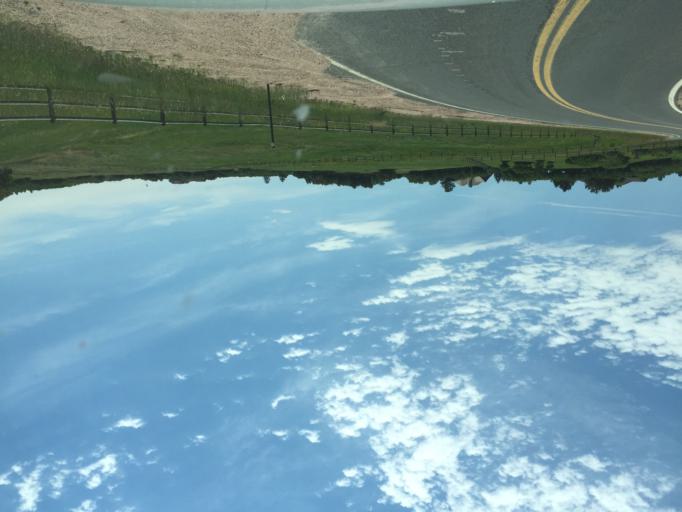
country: US
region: Colorado
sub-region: Douglas County
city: Perry Park
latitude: 39.3074
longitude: -104.9212
